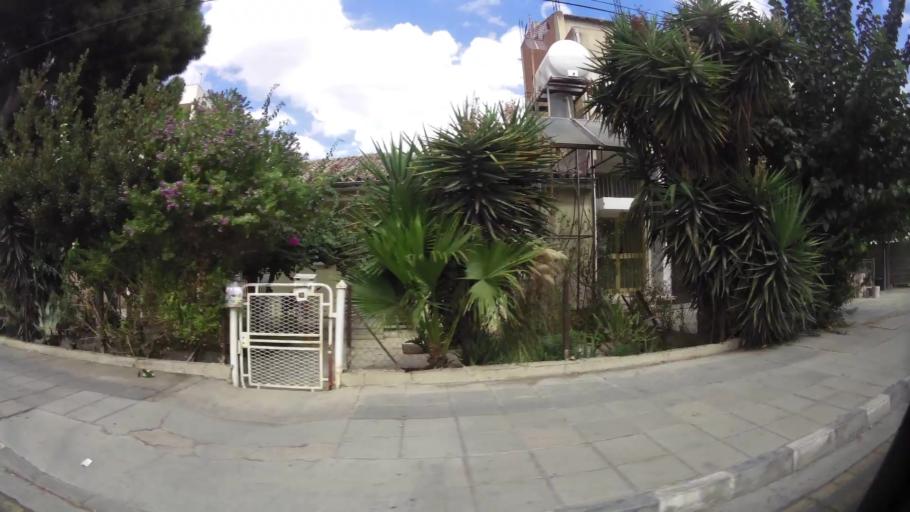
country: CY
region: Lefkosia
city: Nicosia
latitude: 35.1731
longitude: 33.3824
